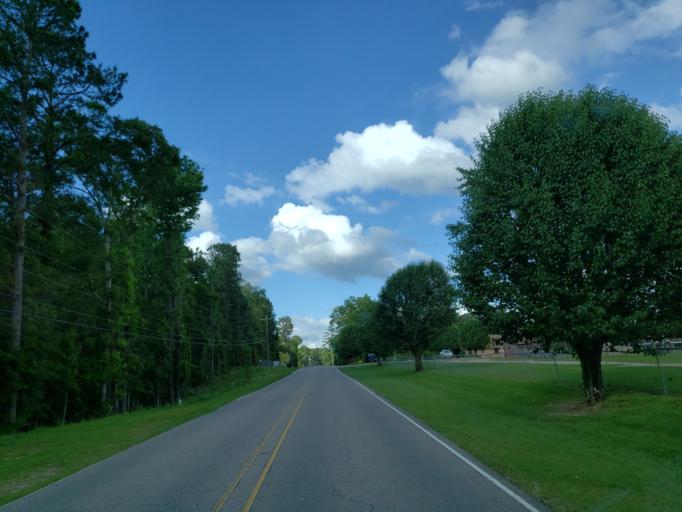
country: US
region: Mississippi
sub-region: Forrest County
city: Petal
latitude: 31.3156
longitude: -89.2108
